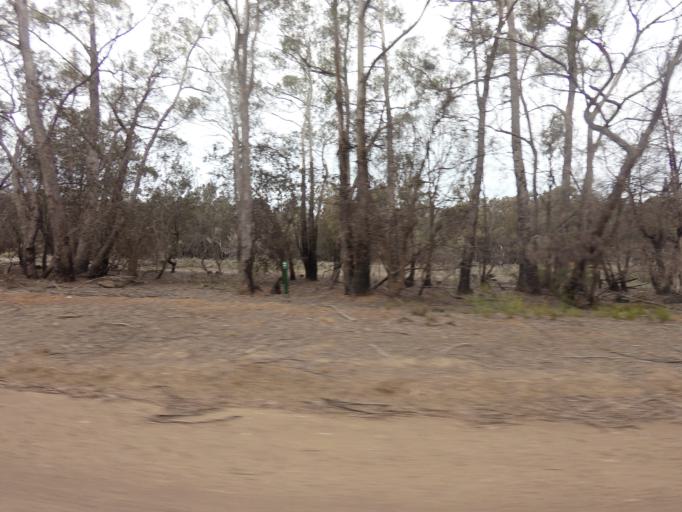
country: AU
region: Tasmania
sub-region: Break O'Day
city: St Helens
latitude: -41.9382
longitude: 148.0735
